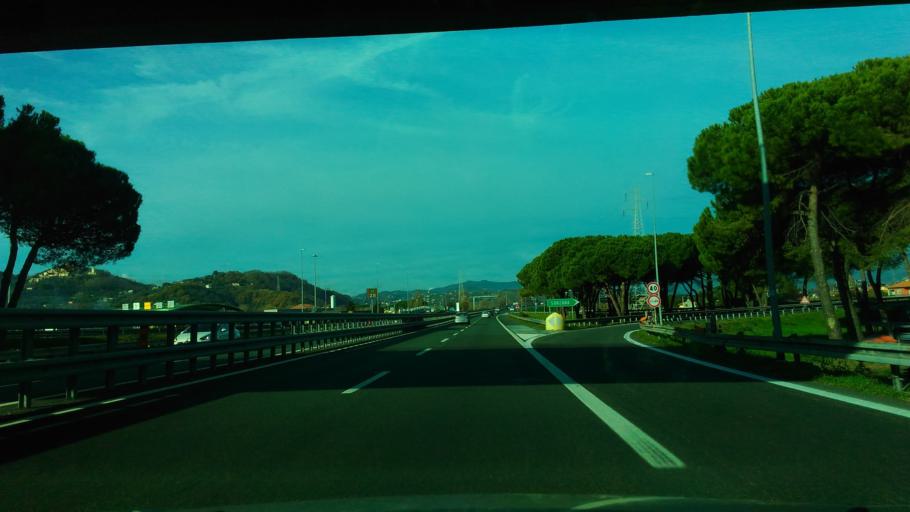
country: IT
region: Liguria
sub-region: Provincia di La Spezia
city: Sarzana
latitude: 44.1011
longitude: 9.9531
